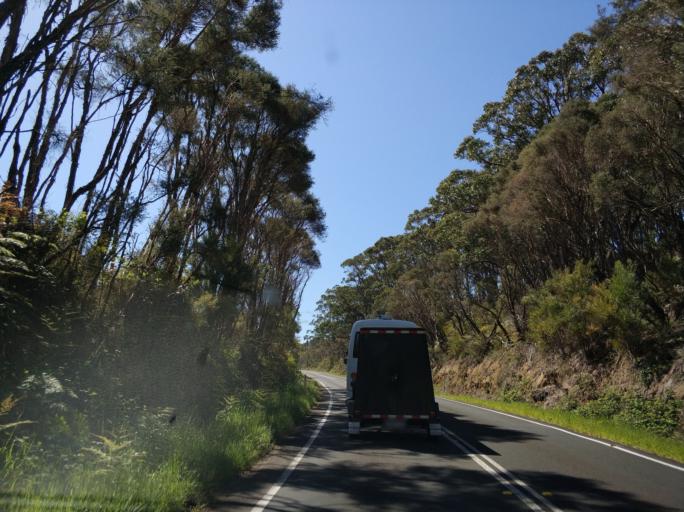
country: AU
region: Victoria
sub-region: Colac-Otway
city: Apollo Bay
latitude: -38.7247
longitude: 143.2481
